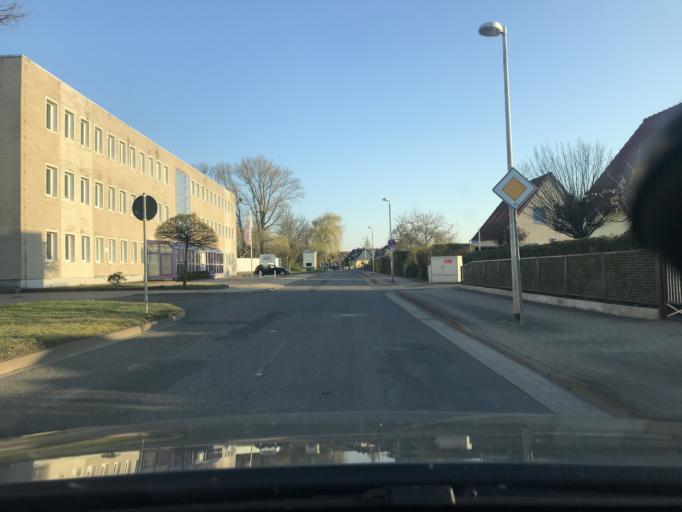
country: DE
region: Thuringia
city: Nordhausen
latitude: 51.4997
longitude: 10.7699
